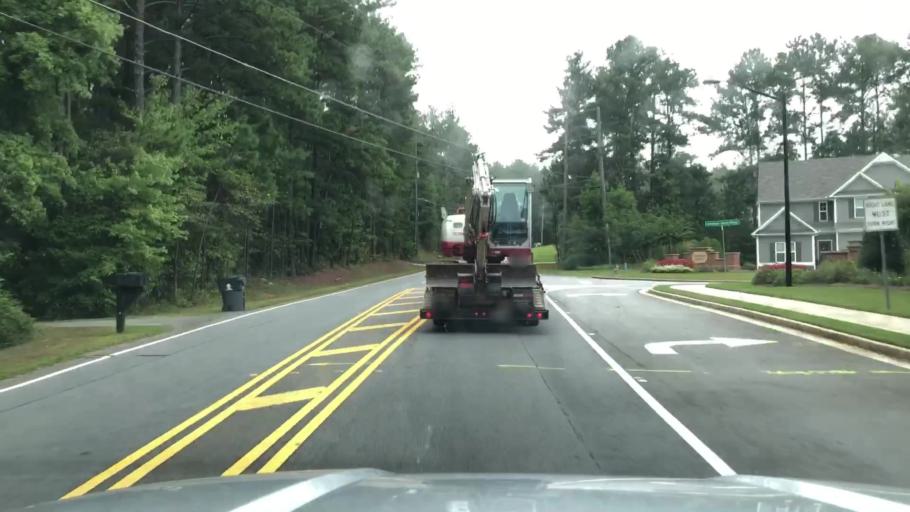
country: US
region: Georgia
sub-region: Bartow County
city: Emerson
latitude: 34.0433
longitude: -84.7743
